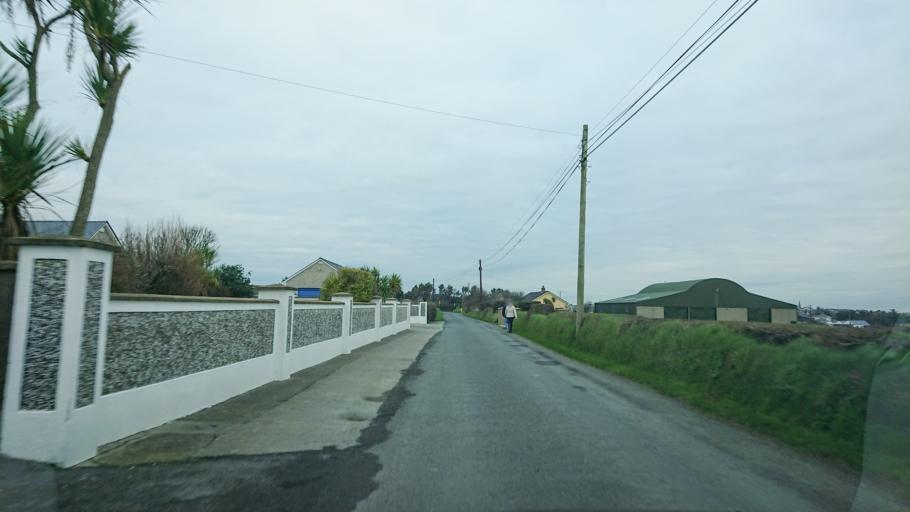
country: IE
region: Munster
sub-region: Waterford
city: Tra Mhor
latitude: 52.1437
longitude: -7.1810
